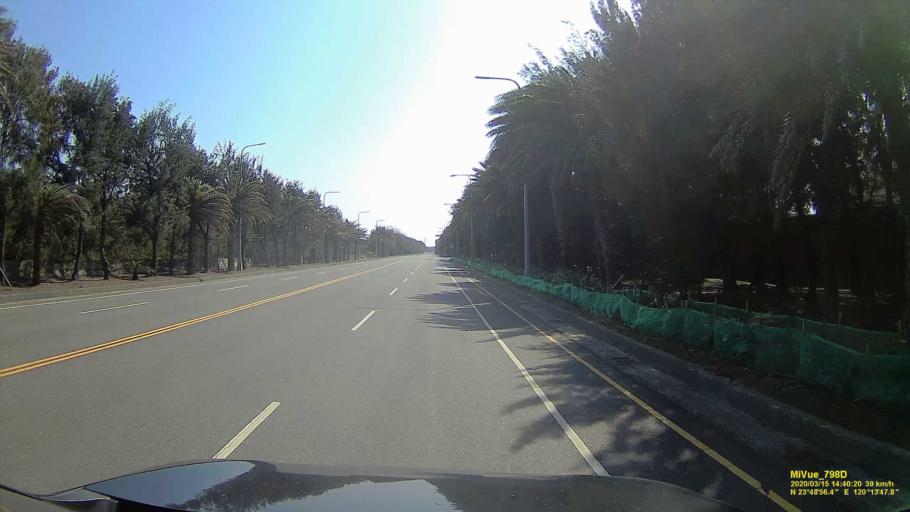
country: TW
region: Taiwan
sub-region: Yunlin
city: Douliu
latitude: 23.8155
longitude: 120.2298
